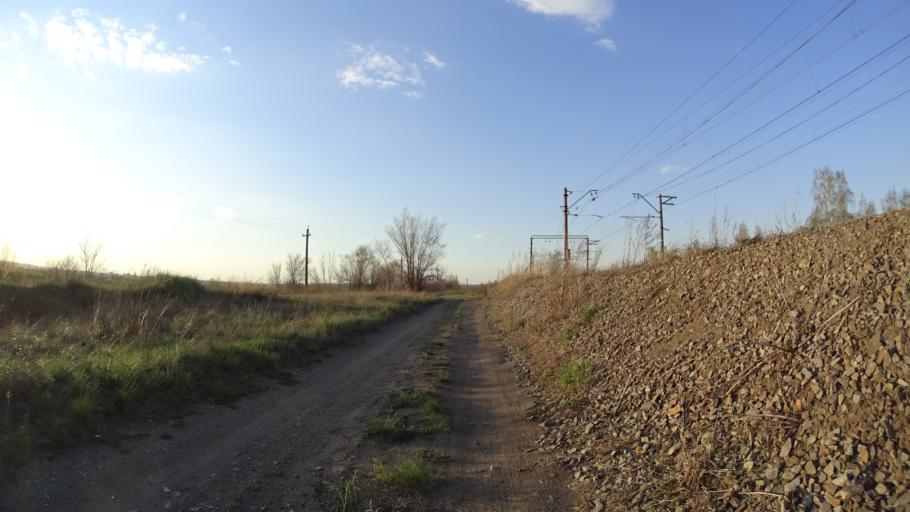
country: RU
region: Chelyabinsk
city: Troitsk
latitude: 54.0611
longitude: 61.6137
